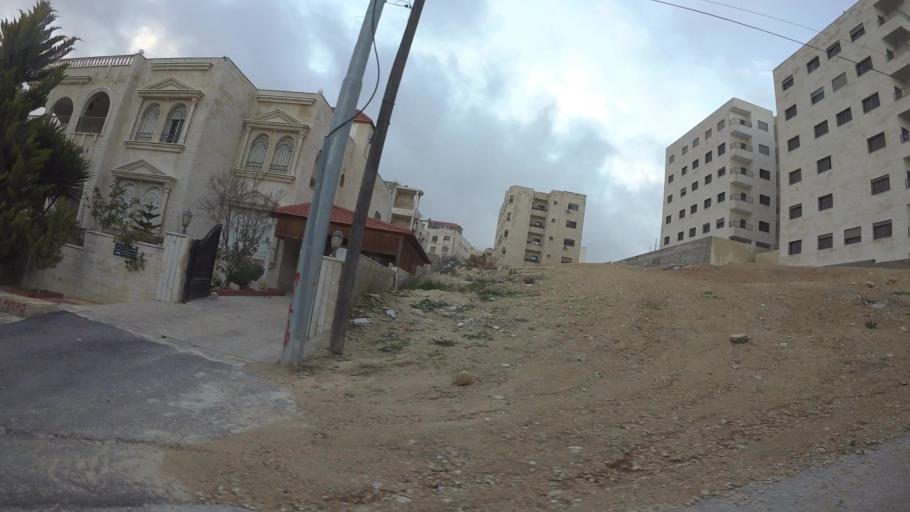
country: JO
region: Amman
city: Al Jubayhah
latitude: 32.0533
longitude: 35.8955
